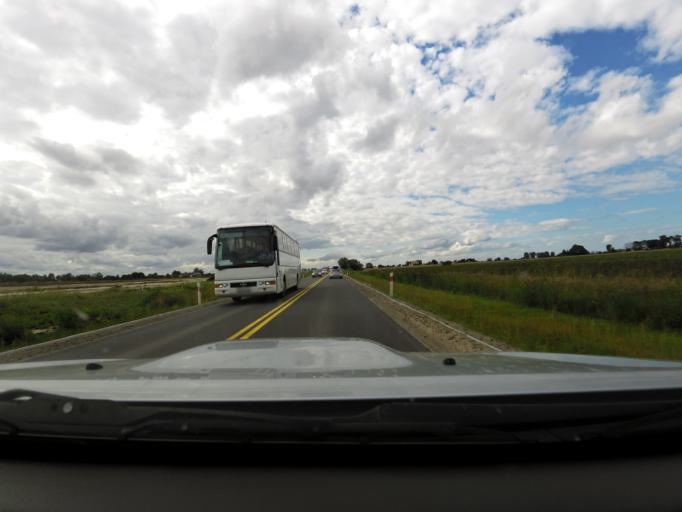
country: PL
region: Pomeranian Voivodeship
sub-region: Powiat nowodworski
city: Nowy Dwor Gdanski
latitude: 54.2190
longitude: 19.0845
